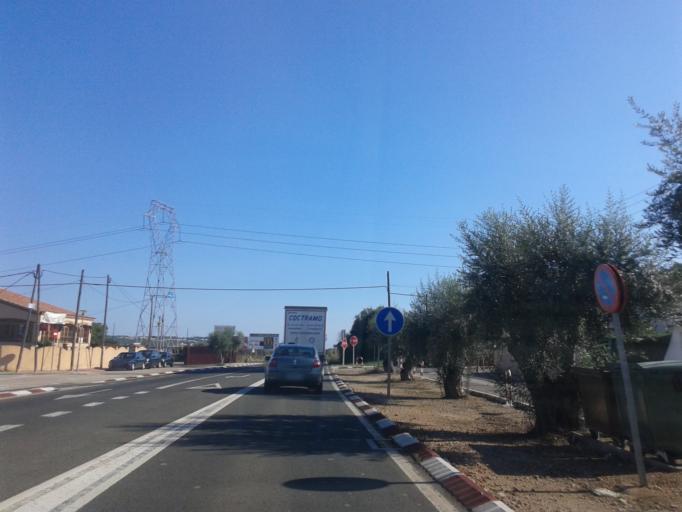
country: ES
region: Catalonia
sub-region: Provincia de Tarragona
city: El Vendrell
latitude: 41.2435
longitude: 1.5215
